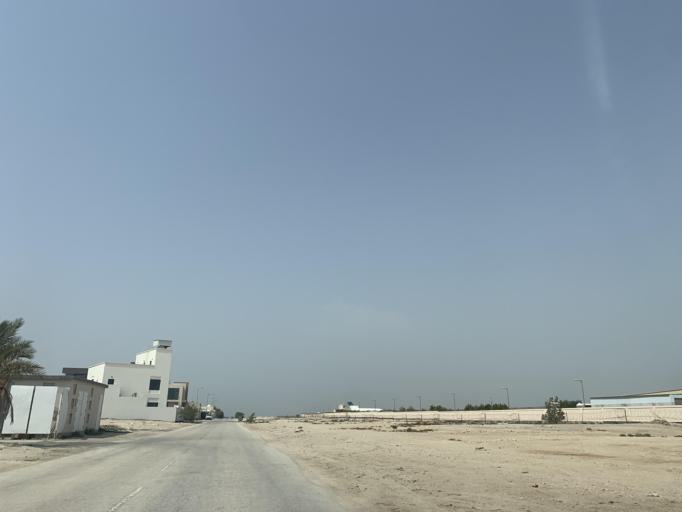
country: BH
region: Central Governorate
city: Madinat Hamad
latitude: 26.1592
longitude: 50.4811
